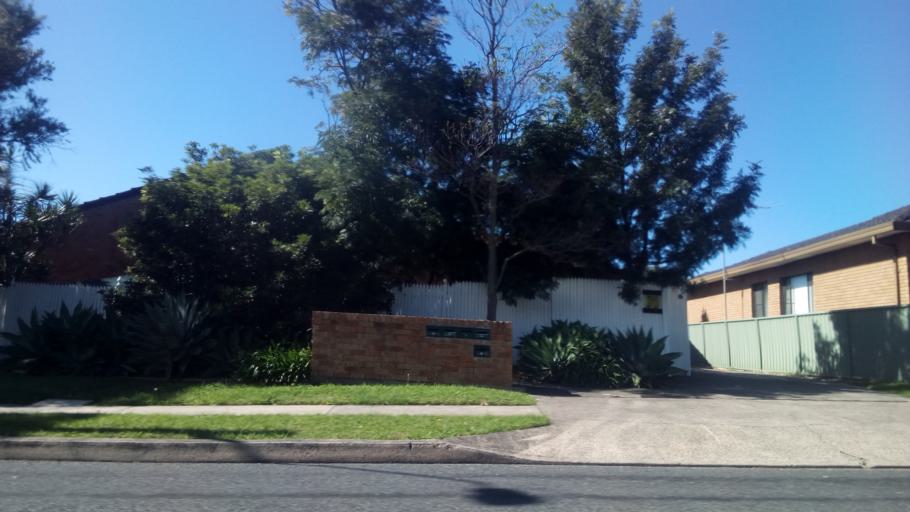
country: AU
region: New South Wales
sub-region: Wollongong
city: East Corrimal
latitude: -34.3665
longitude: 150.9107
